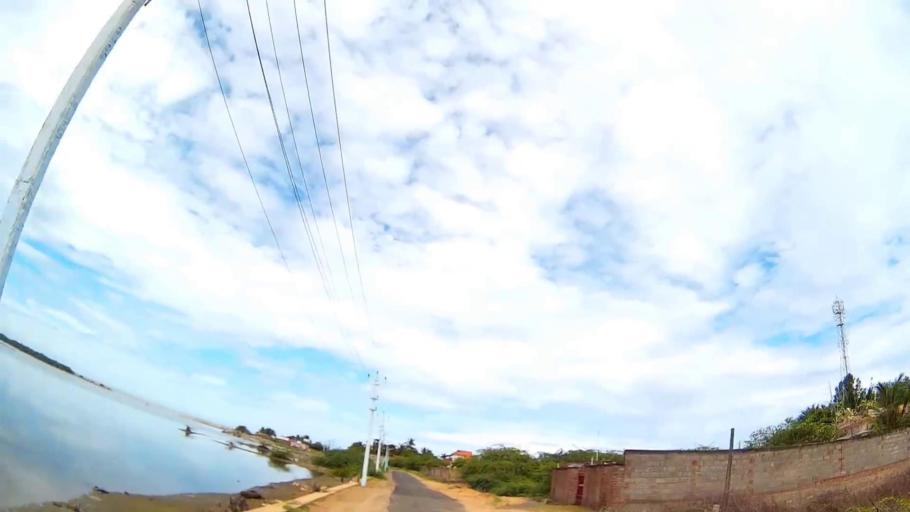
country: IN
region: Tamil Nadu
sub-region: Thoothukkudi
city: Udankudi
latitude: 8.3785
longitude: 78.0533
